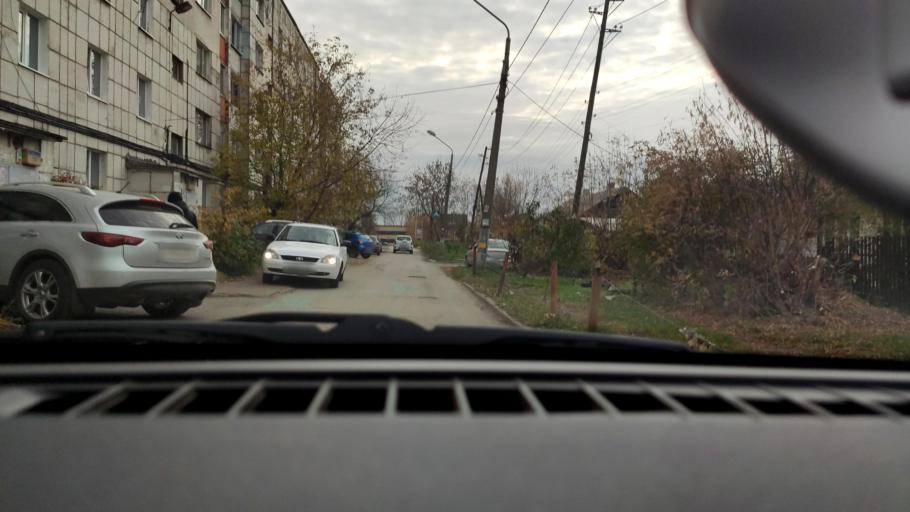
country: RU
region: Perm
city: Kondratovo
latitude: 57.9628
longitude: 56.1670
